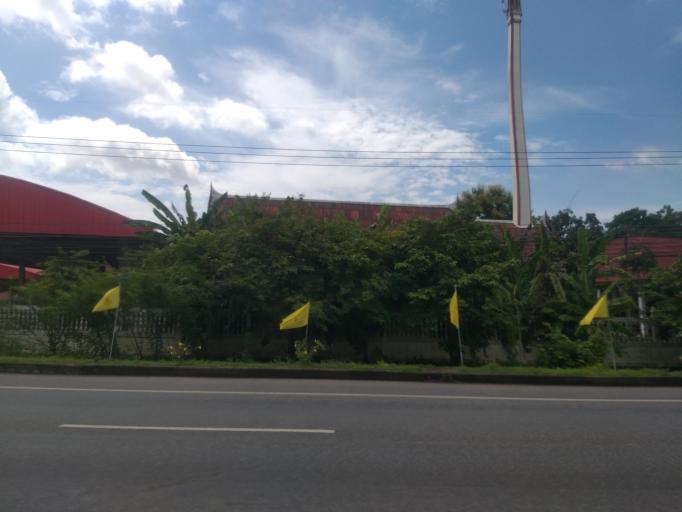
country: TH
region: Nakhon Nayok
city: Nakhon Nayok
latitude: 14.2656
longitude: 101.2707
